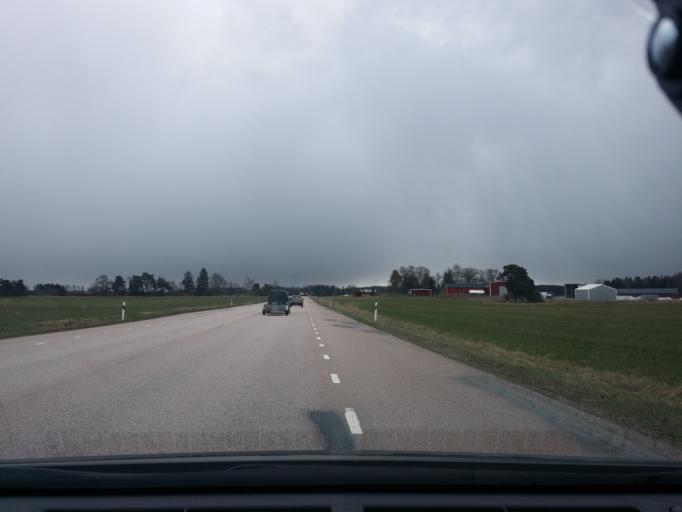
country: SE
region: Uppsala
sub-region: Enkopings Kommun
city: Enkoping
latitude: 59.6890
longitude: 17.0332
